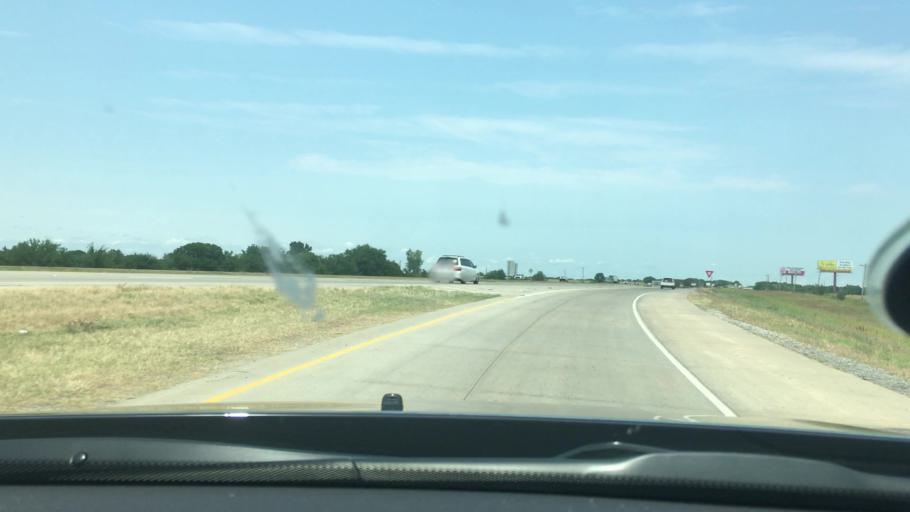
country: US
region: Oklahoma
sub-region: Love County
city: Marietta
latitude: 33.9428
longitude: -97.1346
